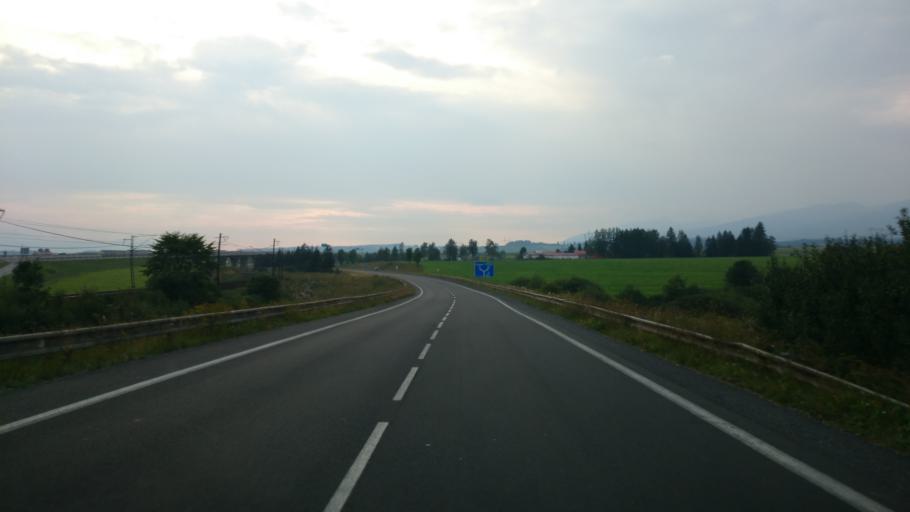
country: SK
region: Presovsky
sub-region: Okres Poprad
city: Strba
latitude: 49.0706
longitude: 19.9984
